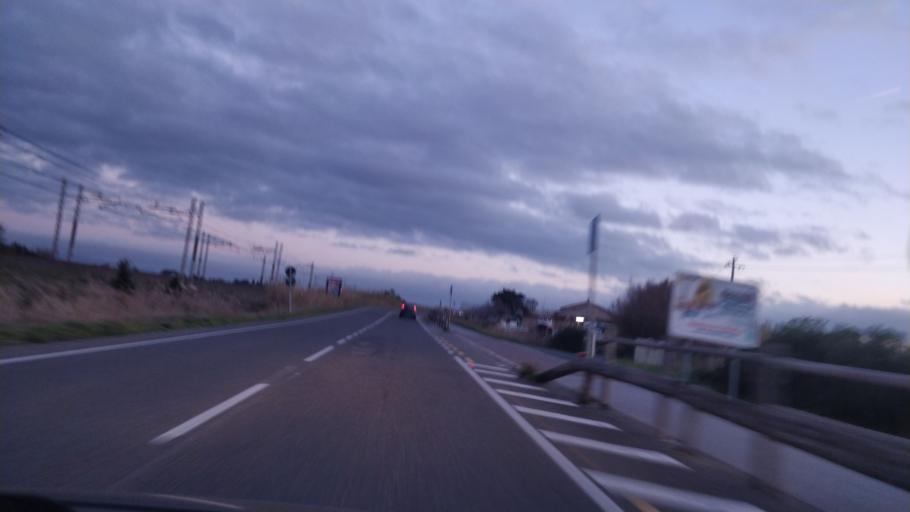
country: IT
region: Tuscany
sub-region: Provincia di Livorno
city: Rosignano Solvay-Castiglioncello
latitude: 43.3738
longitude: 10.4490
